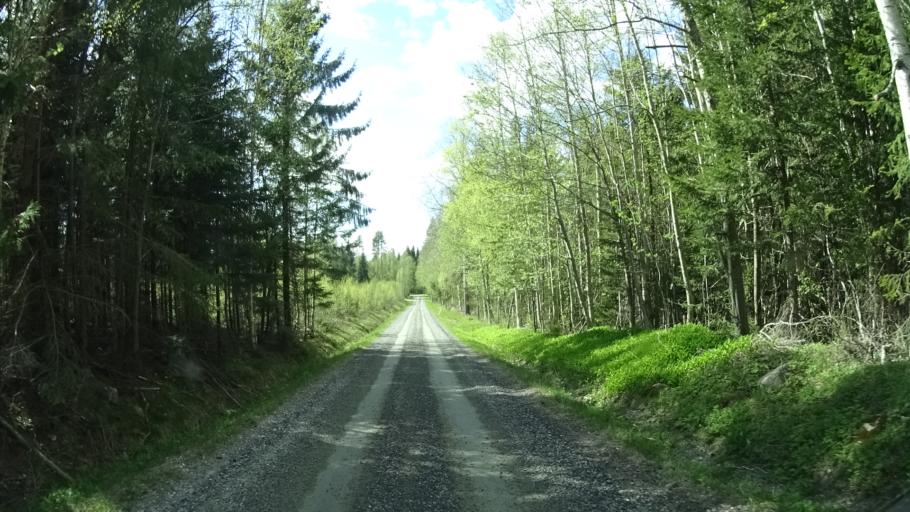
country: SE
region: OErebro
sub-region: Nora Kommun
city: As
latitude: 59.4417
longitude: 14.8401
